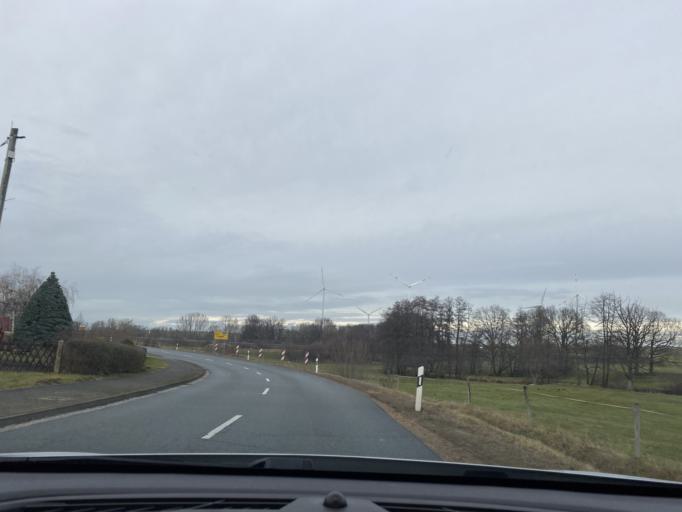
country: DE
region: Saxony
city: Sohland am Rotstein
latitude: 51.1351
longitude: 14.7703
